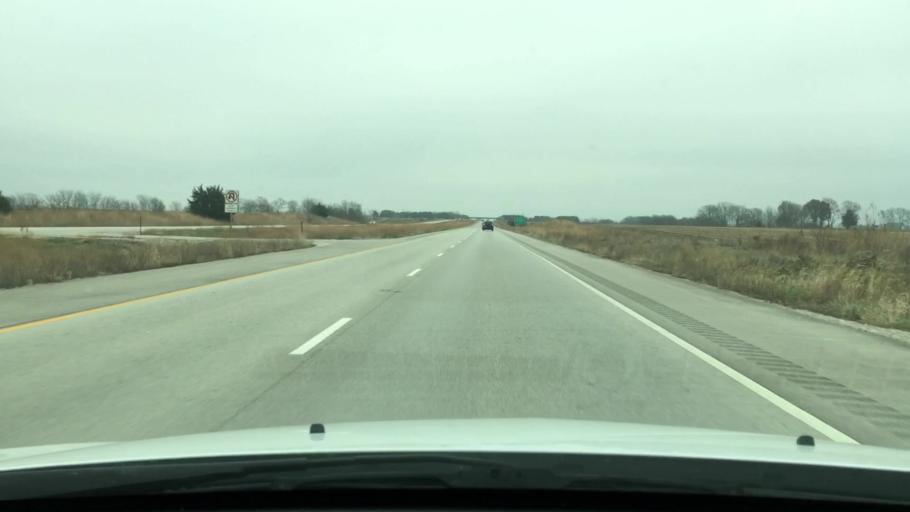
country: US
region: Illinois
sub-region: Sangamon County
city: New Berlin
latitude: 39.7367
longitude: -90.0618
